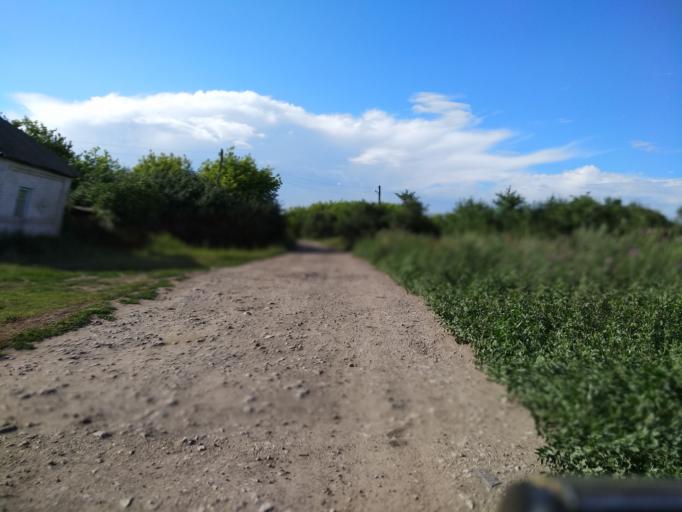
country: RU
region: Lipetsk
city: Dobrinka
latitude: 52.0326
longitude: 40.5629
